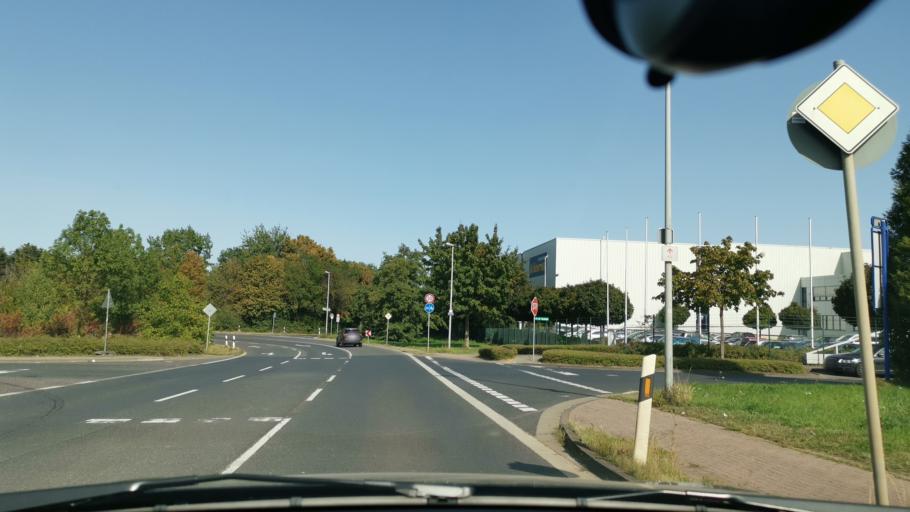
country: DE
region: North Rhine-Westphalia
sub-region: Regierungsbezirk Dusseldorf
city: Neubrueck
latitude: 51.1364
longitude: 6.6196
